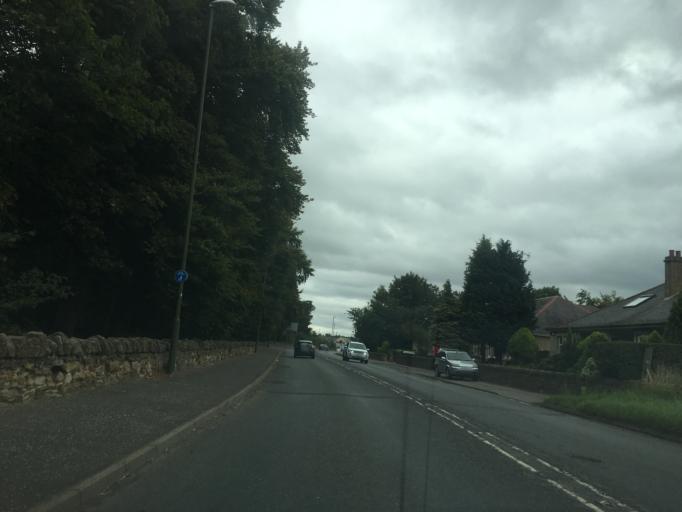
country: GB
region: Scotland
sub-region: Midlothian
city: Bonnyrigg
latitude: 55.8971
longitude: -3.1032
